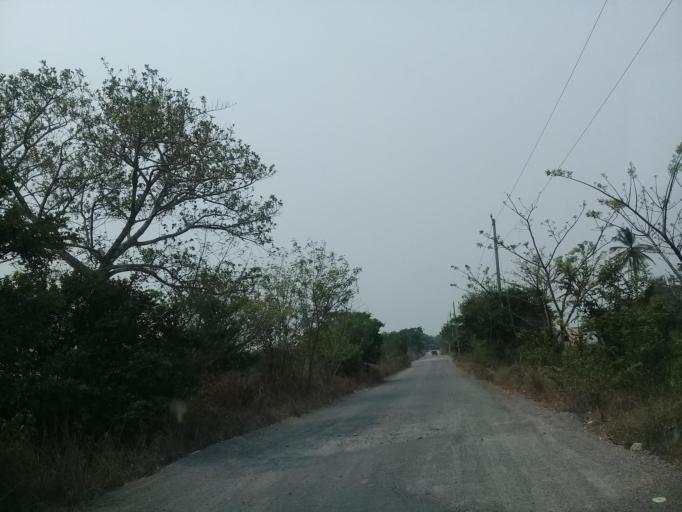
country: MX
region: Veracruz
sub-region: Medellin
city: La Laguna y Monte del Castillo
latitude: 18.9416
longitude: -96.1259
